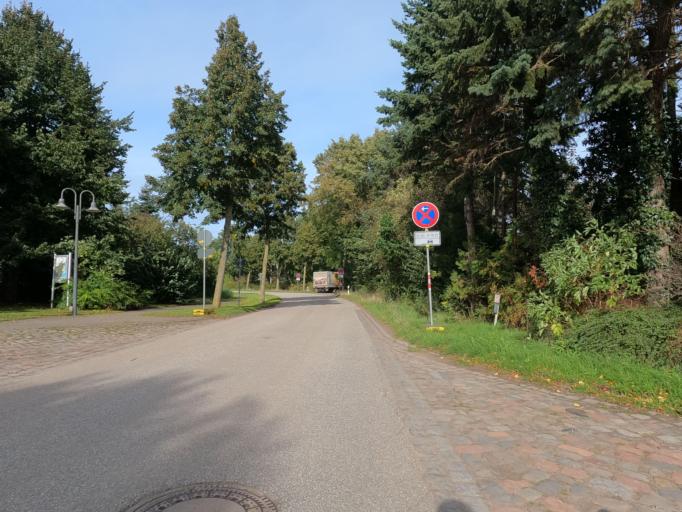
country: DE
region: Schleswig-Holstein
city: Riepsdorf
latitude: 54.2277
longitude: 10.9707
